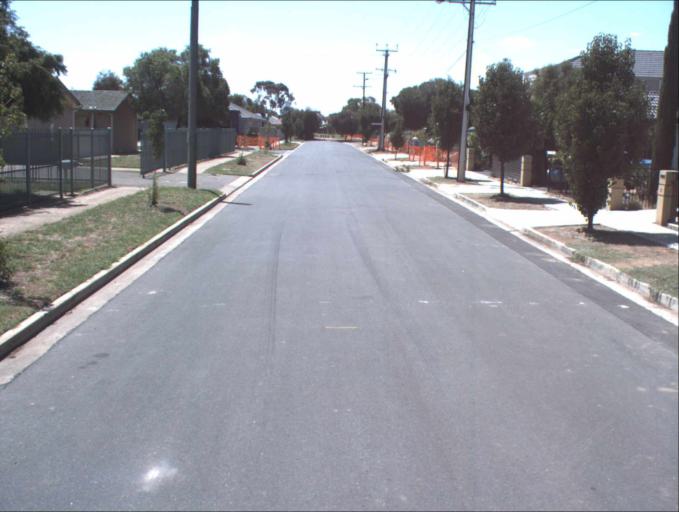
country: AU
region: South Australia
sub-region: Charles Sturt
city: Woodville North
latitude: -34.8578
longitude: 138.5536
